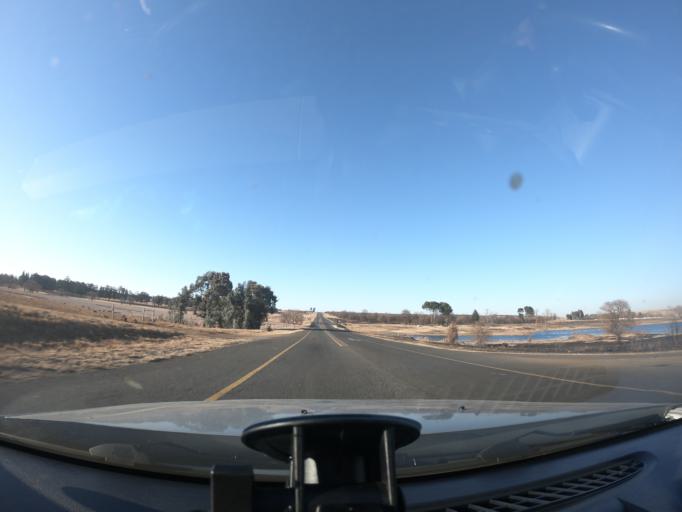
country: ZA
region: Mpumalanga
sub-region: Gert Sibande District Municipality
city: Ermelo
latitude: -26.4637
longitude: 29.9535
